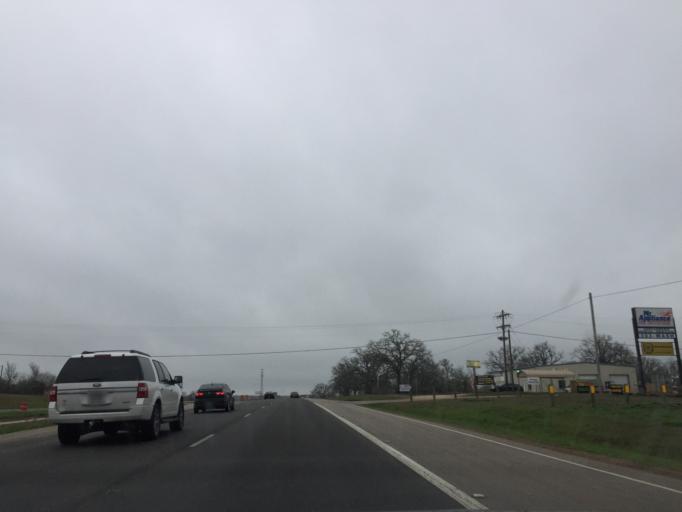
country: US
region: Texas
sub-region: Bastrop County
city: Wyldwood
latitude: 30.1481
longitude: -97.4840
